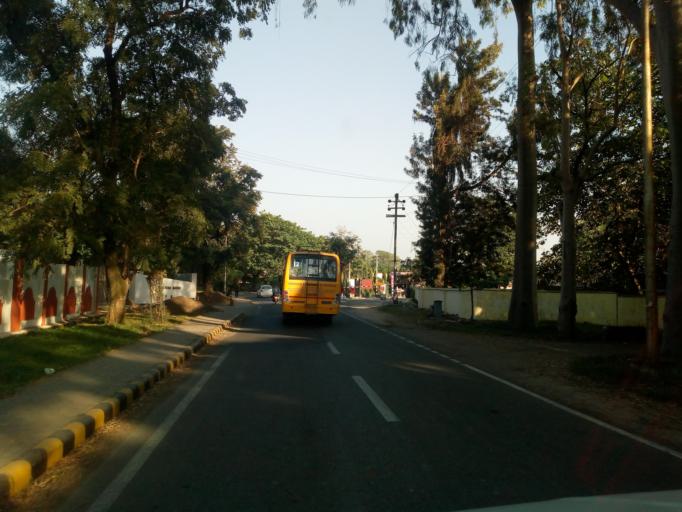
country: IN
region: Uttarakhand
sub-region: Dehradun
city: Dehradun
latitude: 30.3518
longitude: 78.0391
